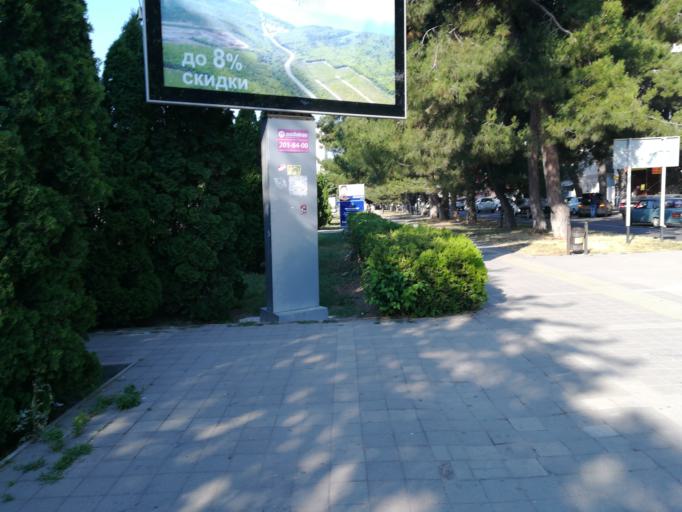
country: RU
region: Krasnodarskiy
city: Anapa
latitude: 44.8980
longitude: 37.3247
